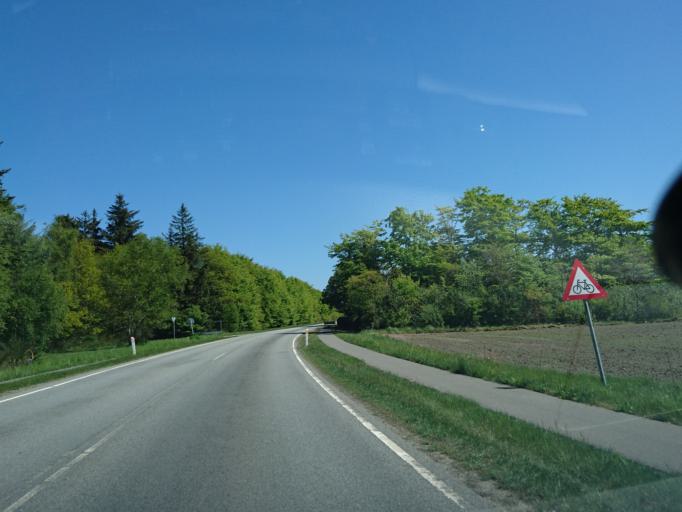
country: DK
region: North Denmark
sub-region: Hjorring Kommune
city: Sindal
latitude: 57.5869
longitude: 10.2301
